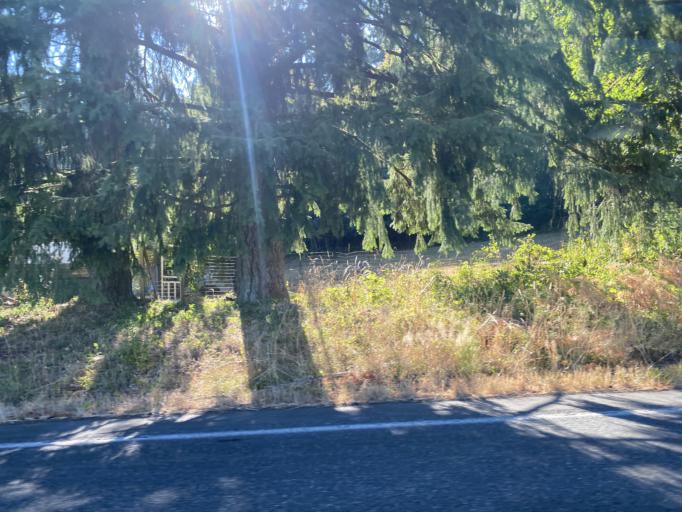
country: US
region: Washington
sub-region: Thurston County
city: Lacey
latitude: 46.9551
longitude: -122.7679
